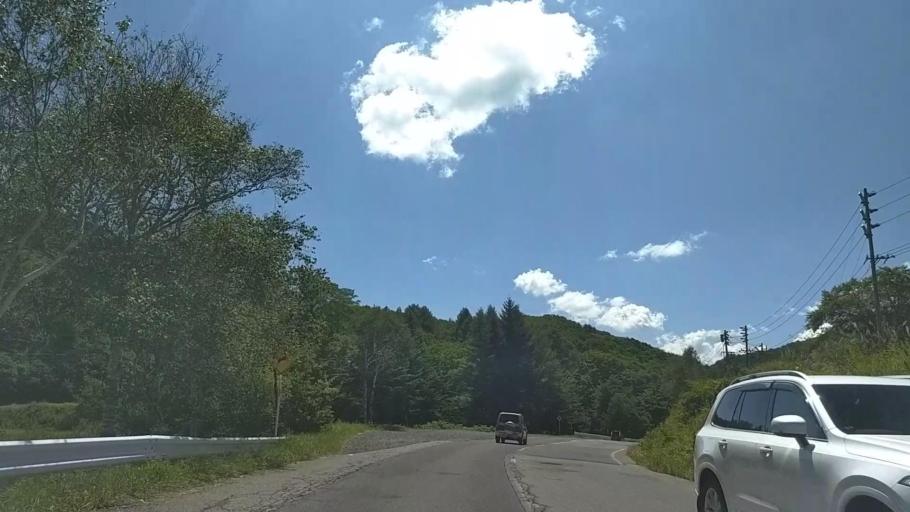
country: JP
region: Nagano
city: Chino
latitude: 36.0998
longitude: 138.2260
